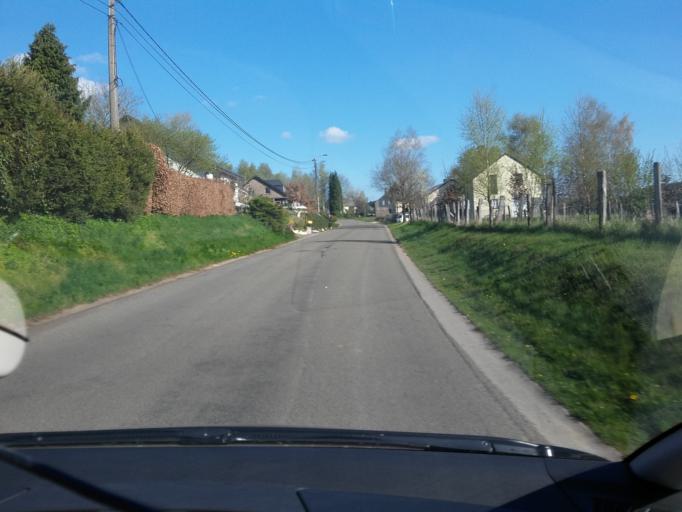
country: BE
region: Wallonia
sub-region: Province du Luxembourg
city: Libin
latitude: 49.9899
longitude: 5.2516
